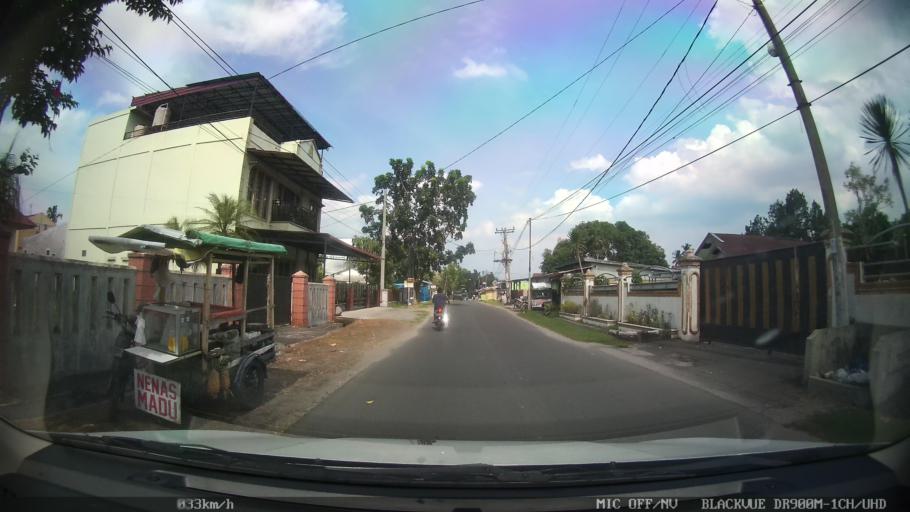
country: ID
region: North Sumatra
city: Binjai
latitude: 3.6131
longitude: 98.5087
